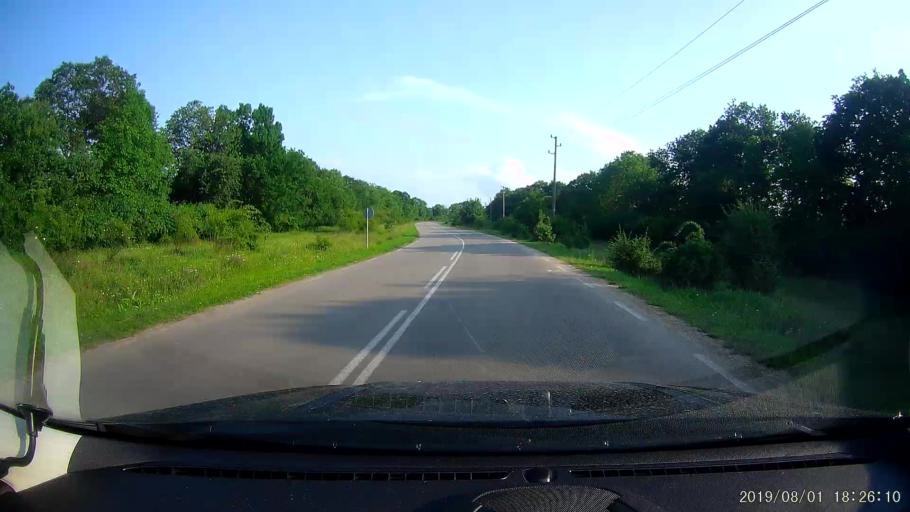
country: BG
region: Shumen
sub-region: Obshtina Venets
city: Venets
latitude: 43.6056
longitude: 26.9945
